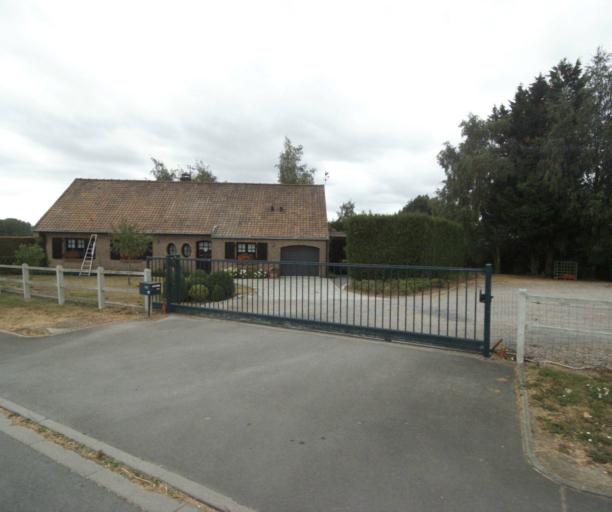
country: FR
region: Nord-Pas-de-Calais
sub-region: Departement du Nord
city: Linselles
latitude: 50.7302
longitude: 3.0923
